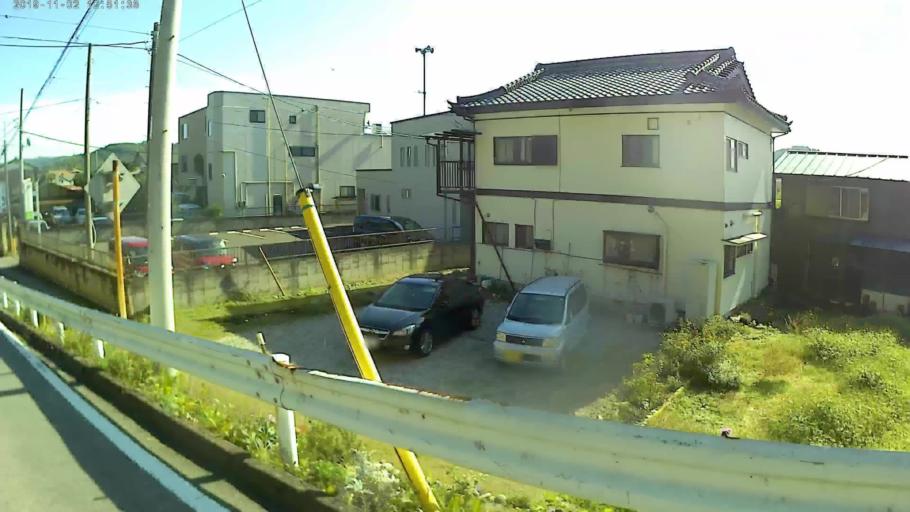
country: JP
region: Gunma
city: Annaka
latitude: 36.3375
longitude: 138.9241
